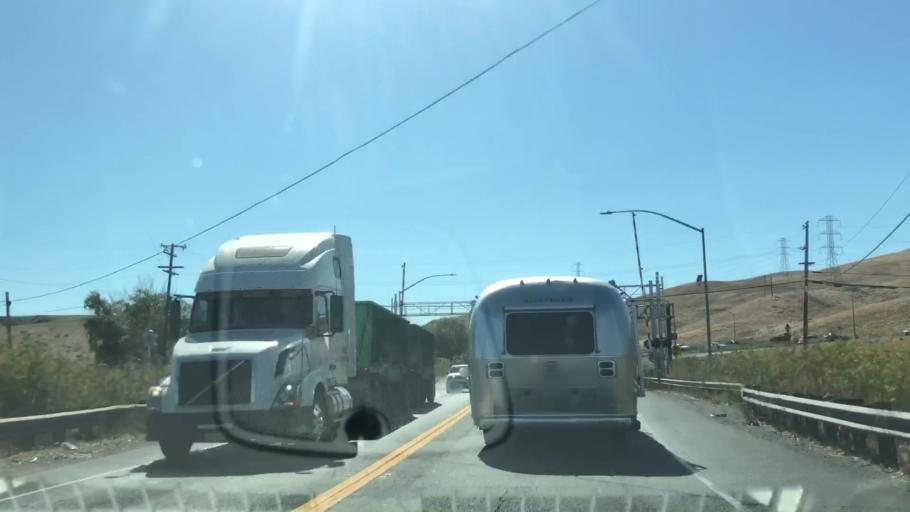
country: US
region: California
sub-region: Marin County
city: Black Point-Green Point
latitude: 38.1517
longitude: -122.4470
